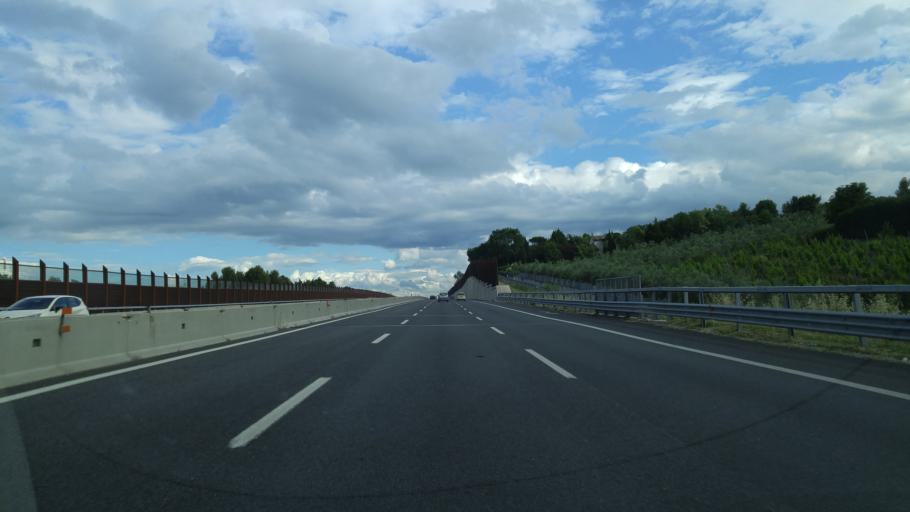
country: IT
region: Emilia-Romagna
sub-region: Provincia di Rimini
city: Rivazzurra
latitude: 44.0235
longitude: 12.5824
